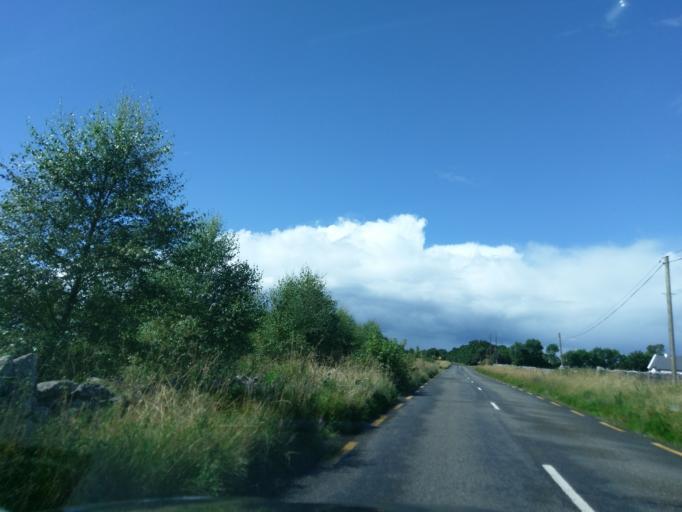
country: IE
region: Connaught
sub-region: County Galway
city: Oranmore
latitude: 53.2811
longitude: -8.8374
